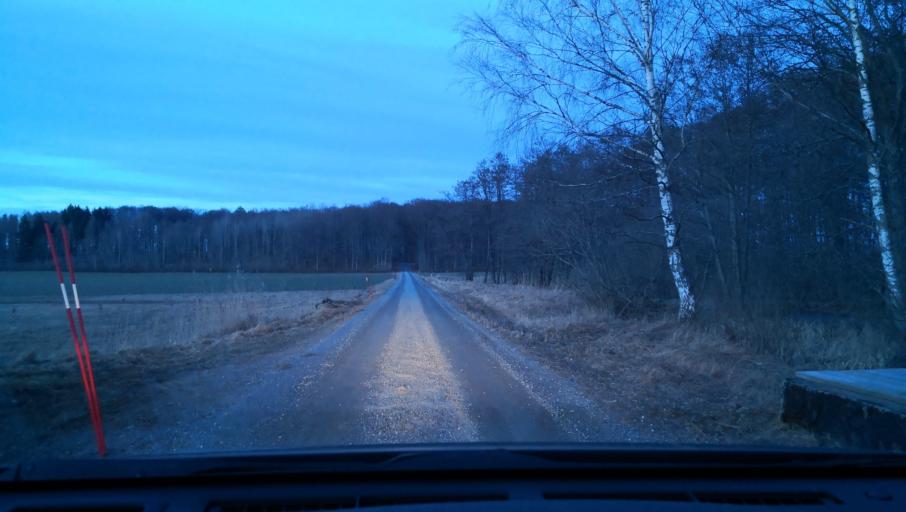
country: SE
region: Uppsala
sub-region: Enkopings Kommun
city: Dalby
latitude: 59.5671
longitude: 17.3751
